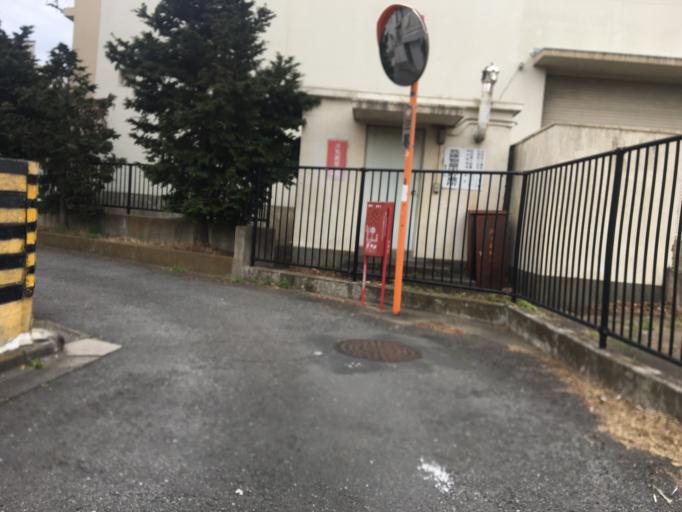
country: JP
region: Tokyo
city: Tokyo
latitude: 35.7158
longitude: 139.6563
